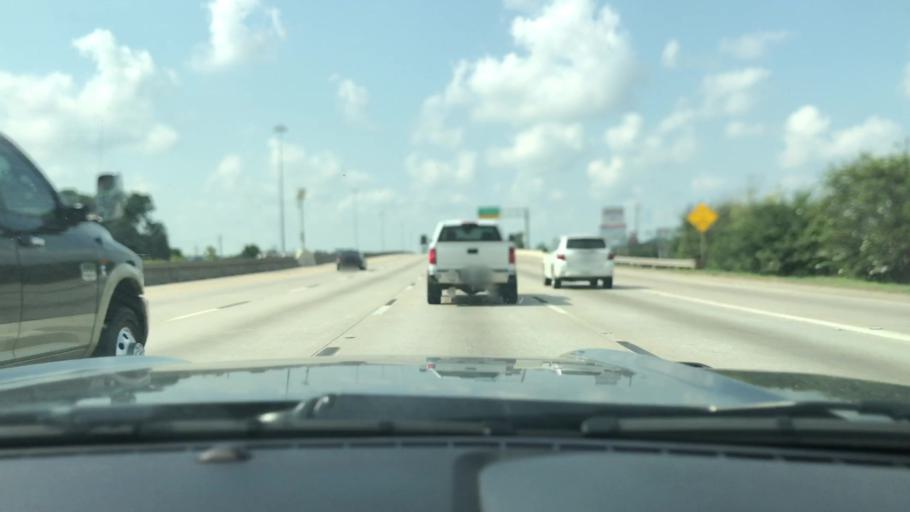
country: US
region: Texas
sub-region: Harris County
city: Aldine
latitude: 29.8941
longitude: -95.3164
